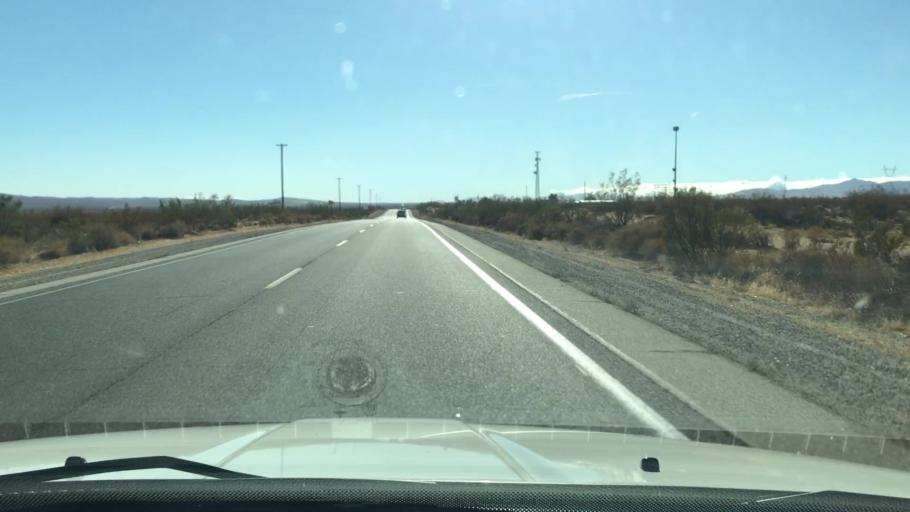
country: US
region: California
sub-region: Kern County
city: Inyokern
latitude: 35.5527
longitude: -117.9255
